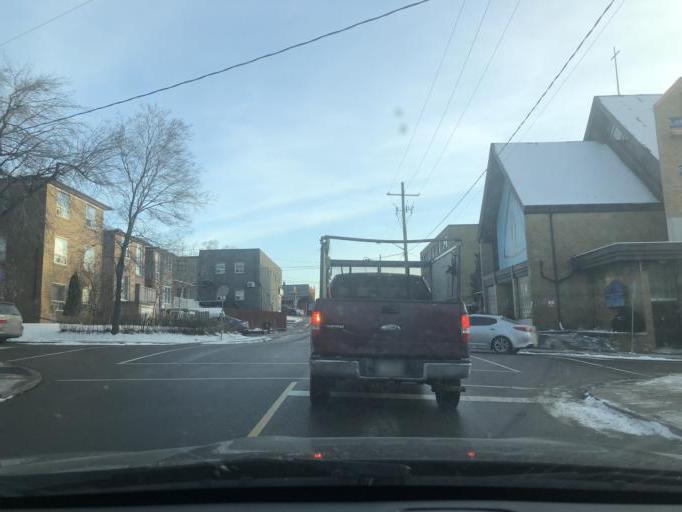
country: CA
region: Ontario
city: Toronto
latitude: 43.6919
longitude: -79.4719
